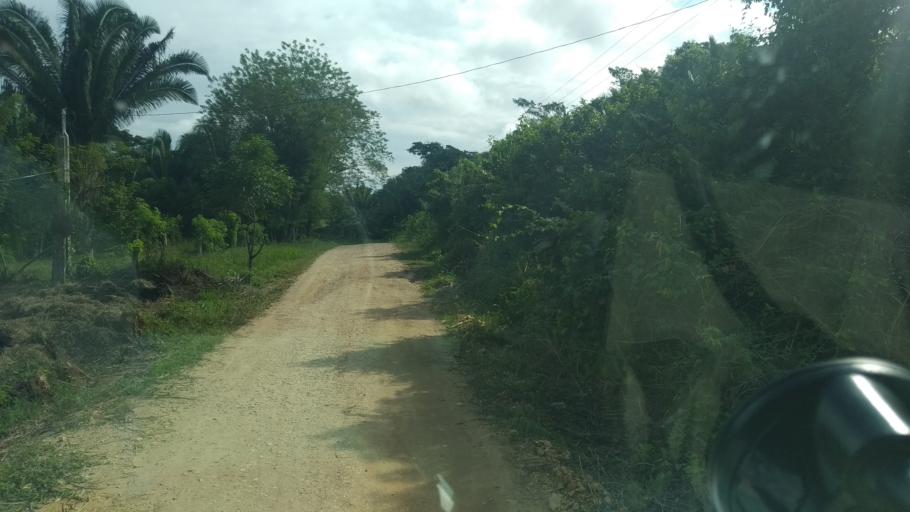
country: BZ
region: Toledo
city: Punta Gorda
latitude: 16.2074
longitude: -88.9155
